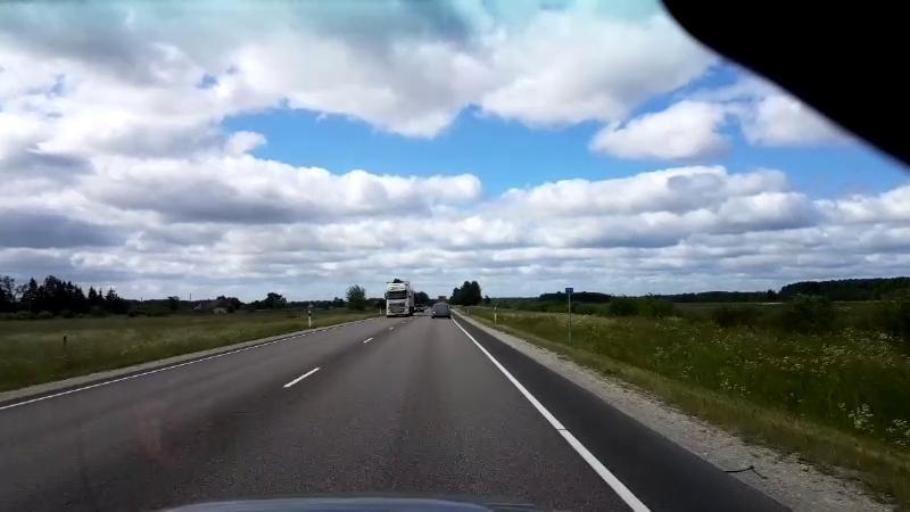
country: EE
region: Paernumaa
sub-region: Sauga vald
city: Sauga
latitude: 58.5081
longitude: 24.5478
